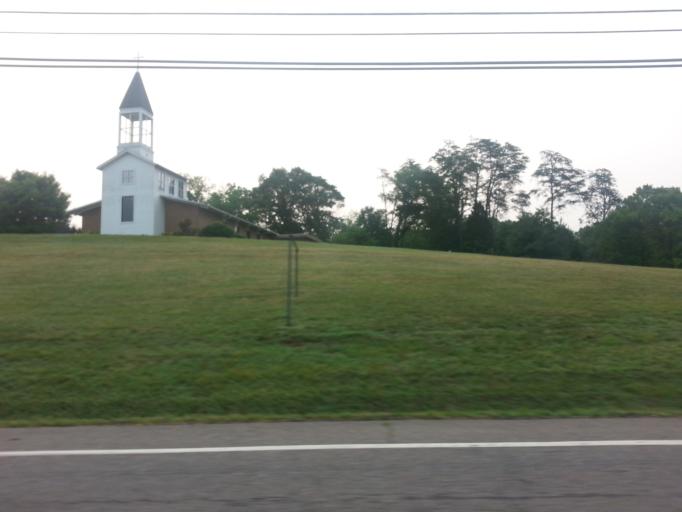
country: US
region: Tennessee
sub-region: Knox County
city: Knoxville
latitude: 35.8858
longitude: -83.9377
